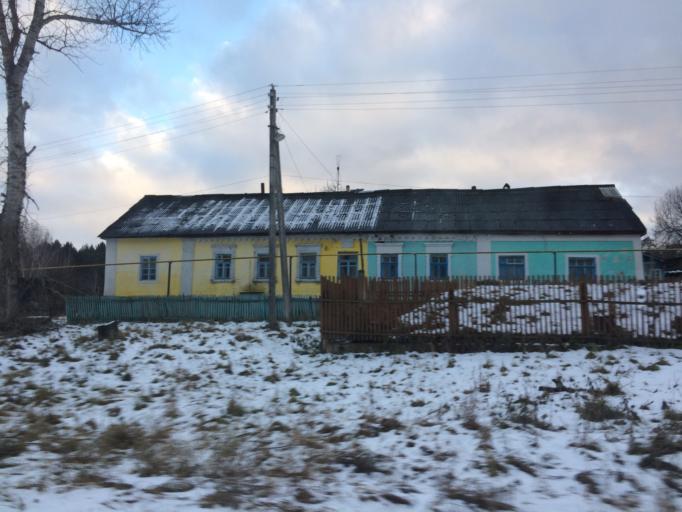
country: RU
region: Tula
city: Cherepet'
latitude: 54.1156
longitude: 36.3523
